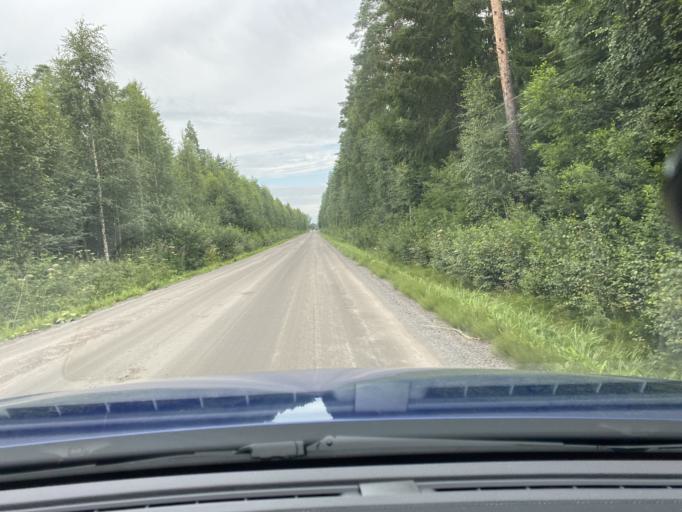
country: FI
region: Satakunta
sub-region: Rauma
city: Kiukainen
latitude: 61.1399
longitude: 21.9939
